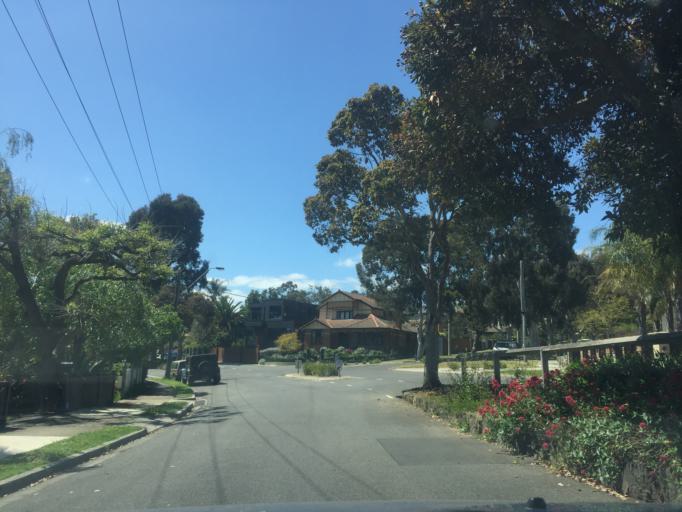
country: AU
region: Victoria
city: Ivanhoe East
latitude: -37.7703
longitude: 145.0515
